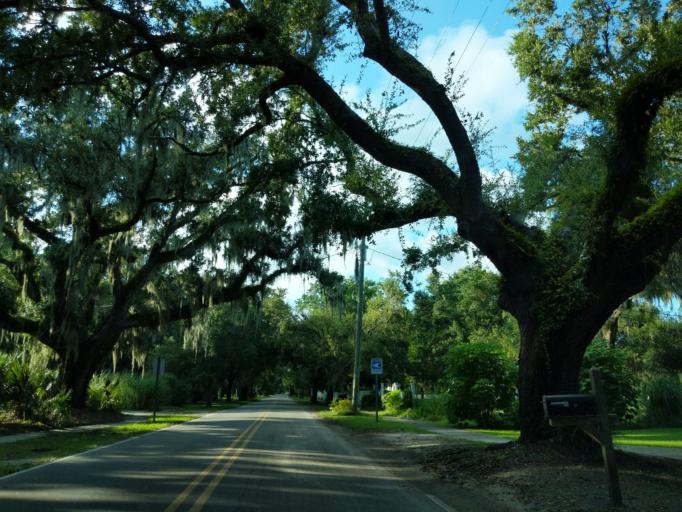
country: US
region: South Carolina
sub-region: Charleston County
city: Awendaw
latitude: 33.0815
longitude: -79.4587
